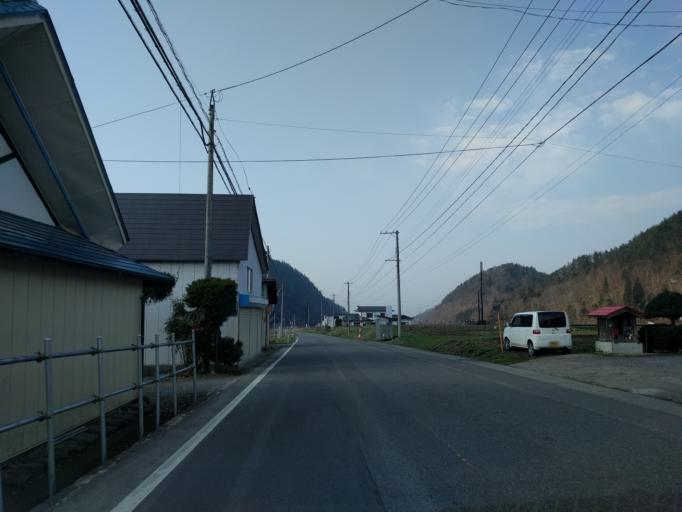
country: JP
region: Fukushima
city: Kitakata
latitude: 37.7000
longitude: 139.9135
